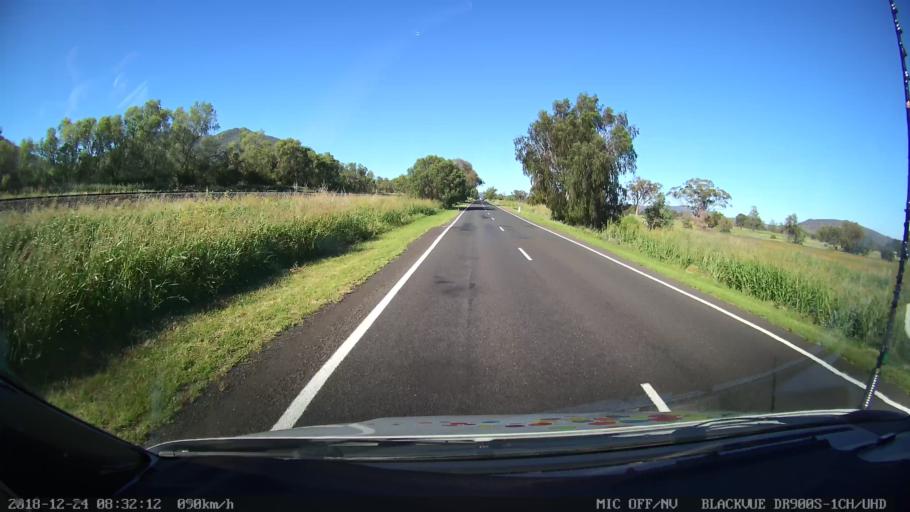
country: AU
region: New South Wales
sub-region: Tamworth Municipality
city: Phillip
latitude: -31.2785
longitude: 150.7012
